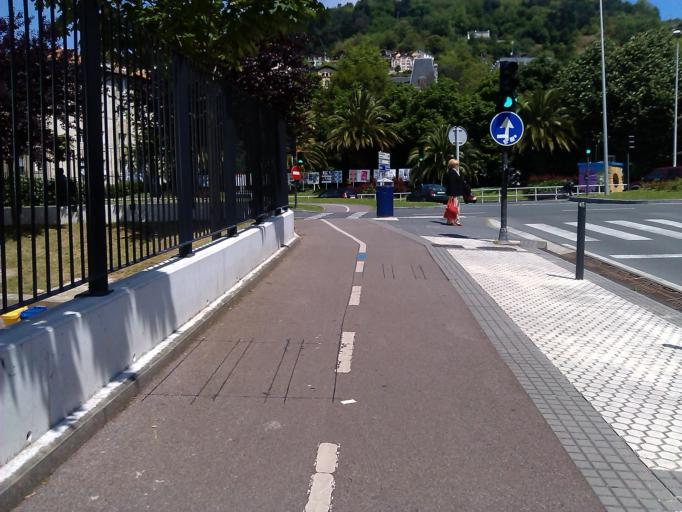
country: ES
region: Basque Country
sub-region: Provincia de Guipuzcoa
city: San Sebastian
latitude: 43.3216
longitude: -1.9608
